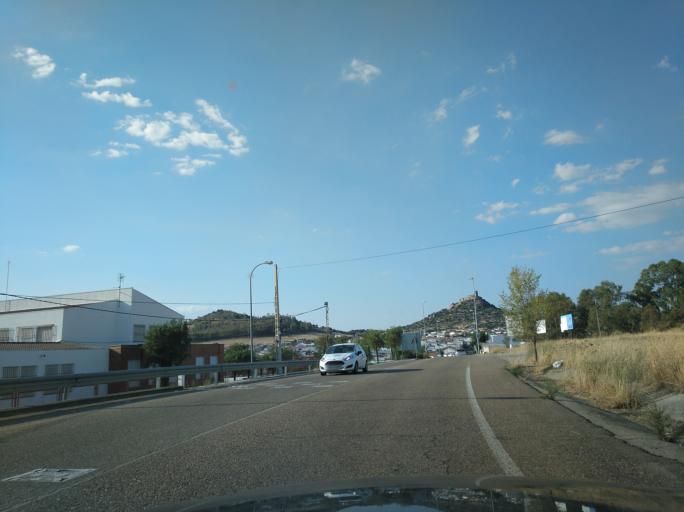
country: ES
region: Extremadura
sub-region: Provincia de Badajoz
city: Alconchel
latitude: 38.5101
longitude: -7.0701
